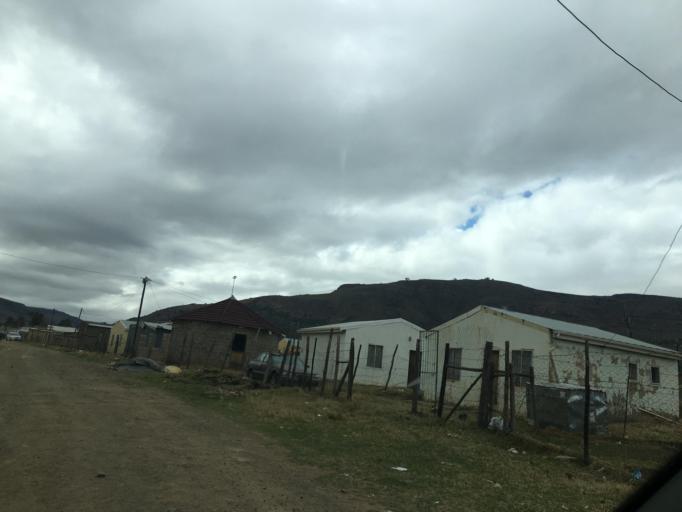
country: ZA
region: Eastern Cape
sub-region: Chris Hani District Municipality
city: Cala
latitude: -31.5355
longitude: 27.7001
